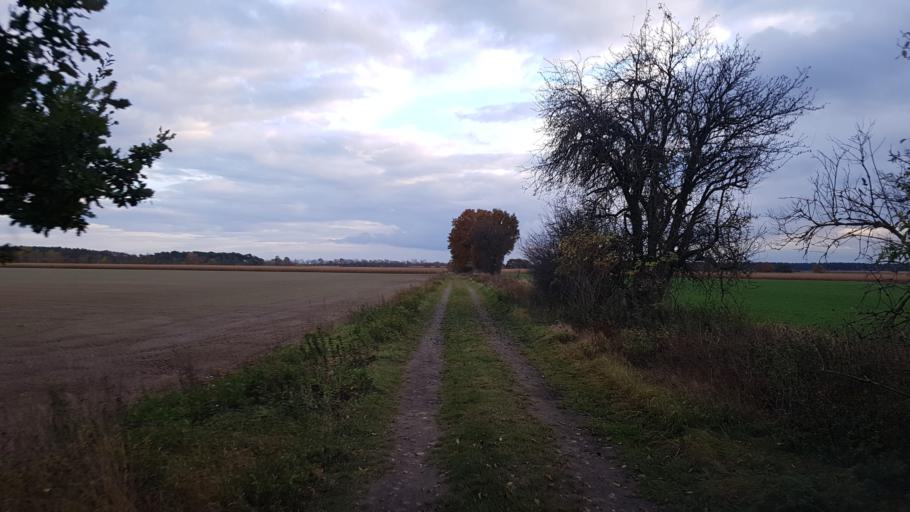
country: DE
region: Saxony-Anhalt
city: Seyda
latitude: 51.9387
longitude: 12.8761
